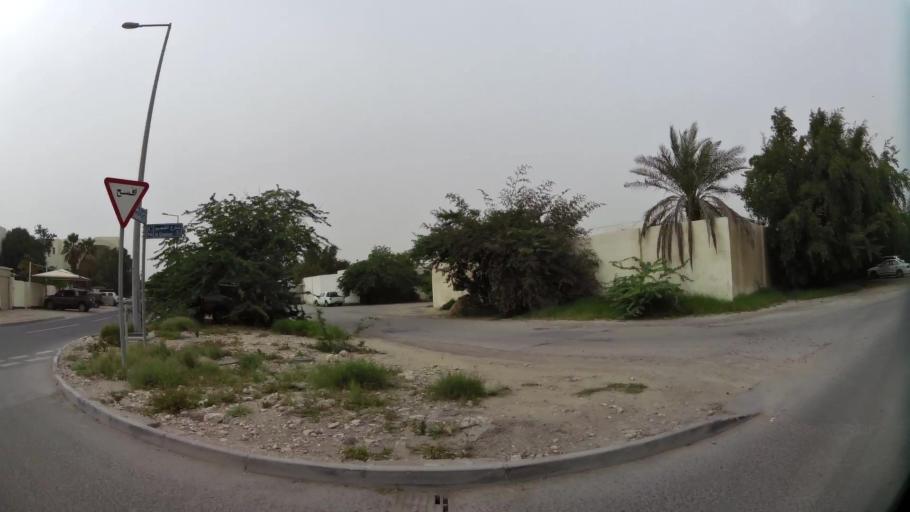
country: QA
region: Baladiyat ad Dawhah
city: Doha
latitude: 25.2551
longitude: 51.4959
